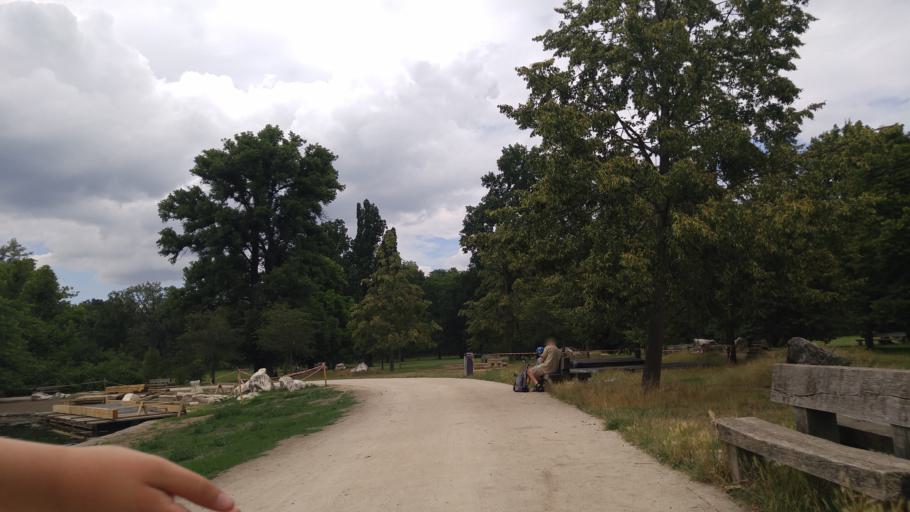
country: CZ
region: Praha
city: Prague
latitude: 50.1069
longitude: 14.4220
